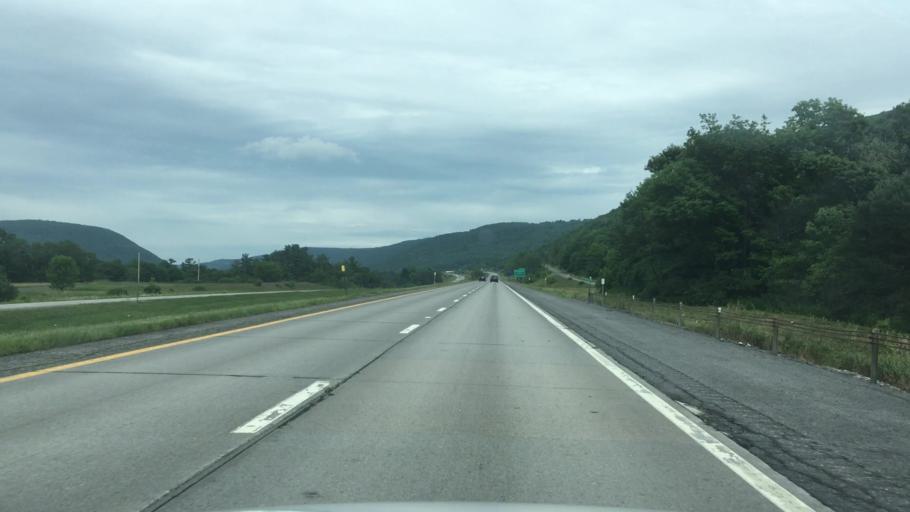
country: US
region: New York
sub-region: Otsego County
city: Worcester
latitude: 42.5366
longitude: -74.8422
